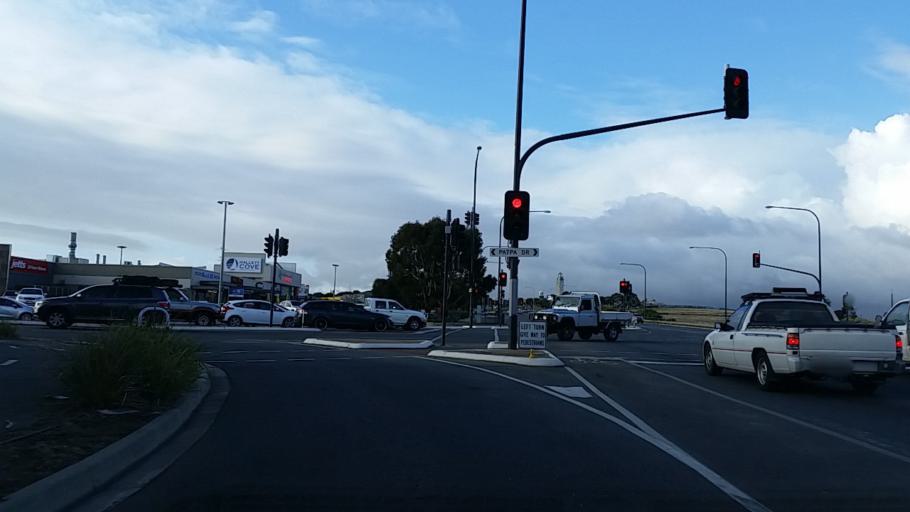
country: AU
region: South Australia
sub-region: Marion
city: Happy Valley
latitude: -35.0795
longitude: 138.5161
